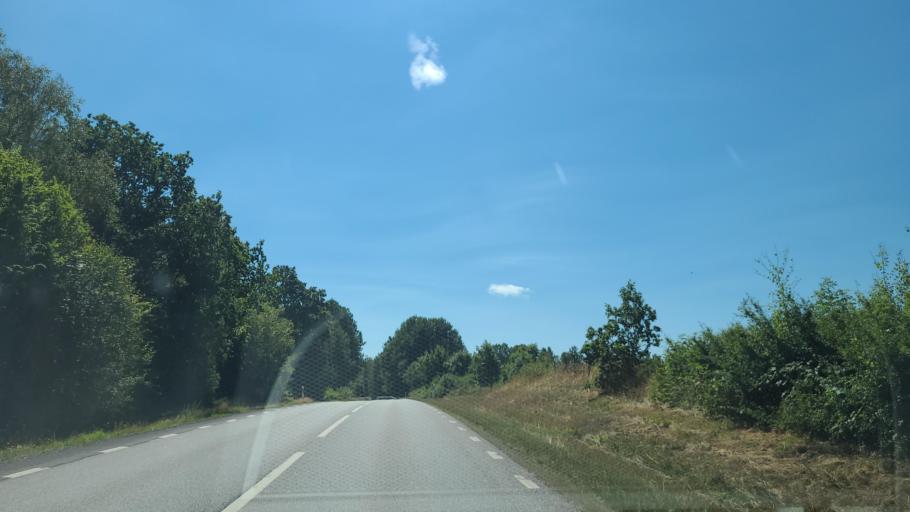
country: SE
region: Blekinge
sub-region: Karlskrona Kommun
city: Rodeby
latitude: 56.3025
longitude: 15.5815
